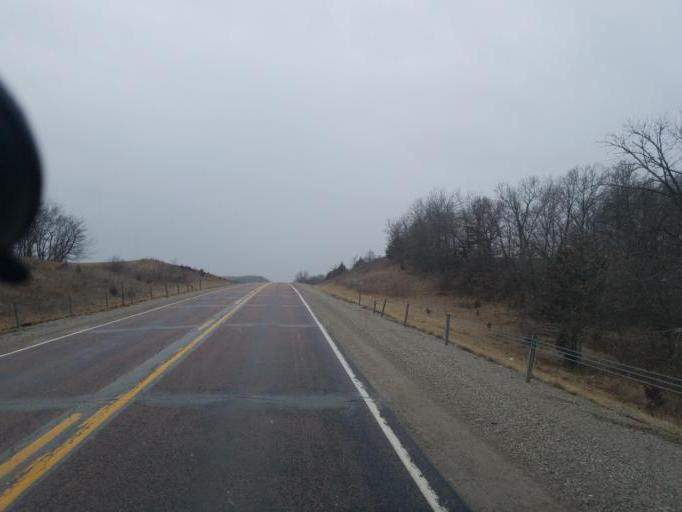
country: US
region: Iowa
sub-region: Appanoose County
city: Centerville
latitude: 40.6168
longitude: -92.9562
